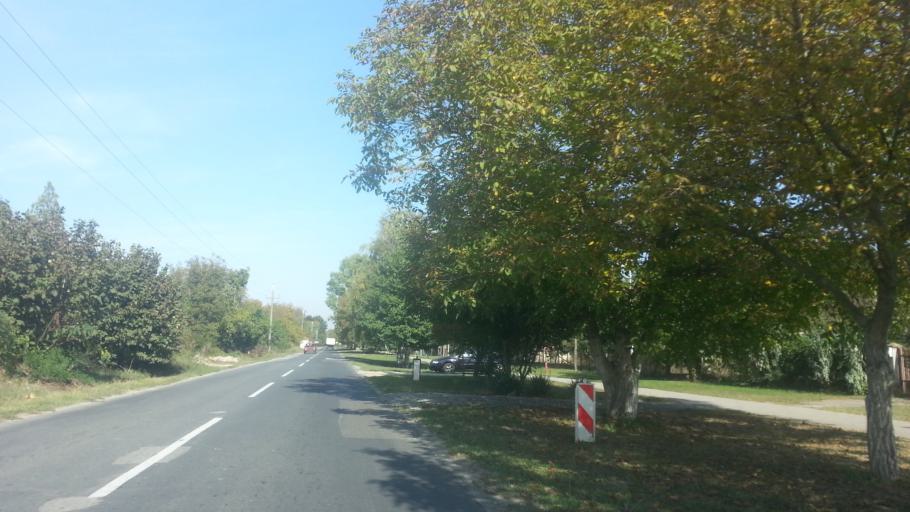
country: RS
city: Stari Banovci
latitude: 44.9988
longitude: 20.2994
